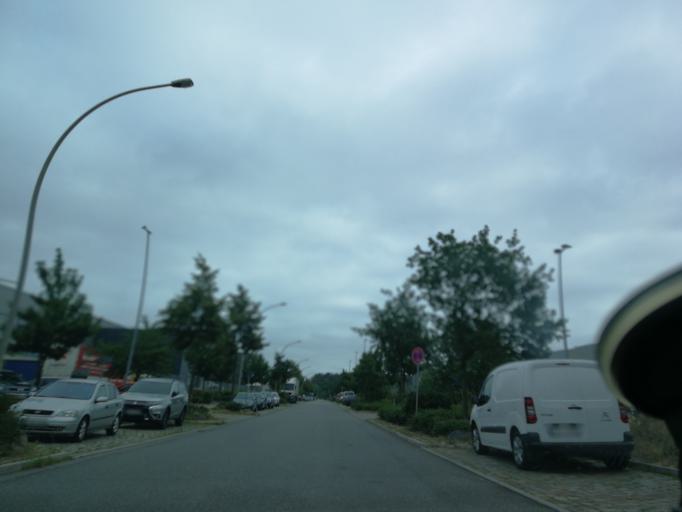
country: DE
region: Hamburg
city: Altona
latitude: 53.5048
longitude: 9.9259
